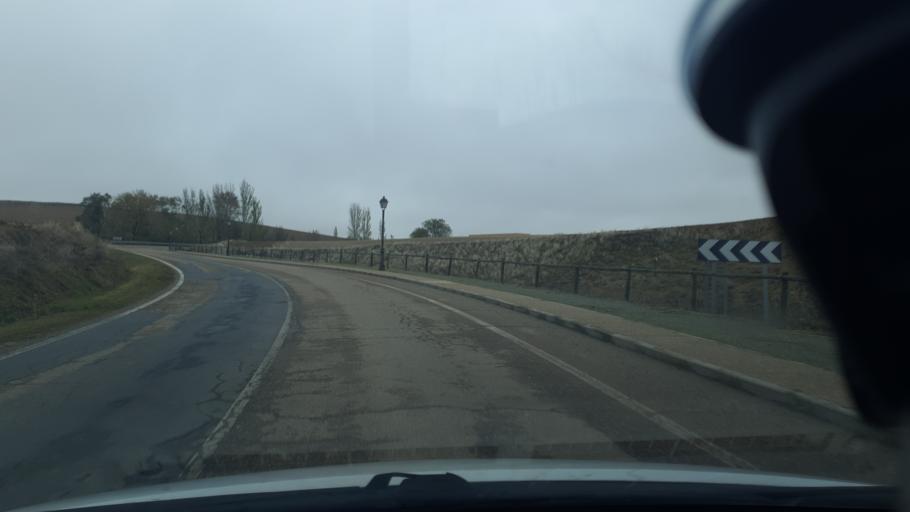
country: ES
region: Castille and Leon
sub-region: Provincia de Segovia
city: Valseca
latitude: 41.0020
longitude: -4.1661
